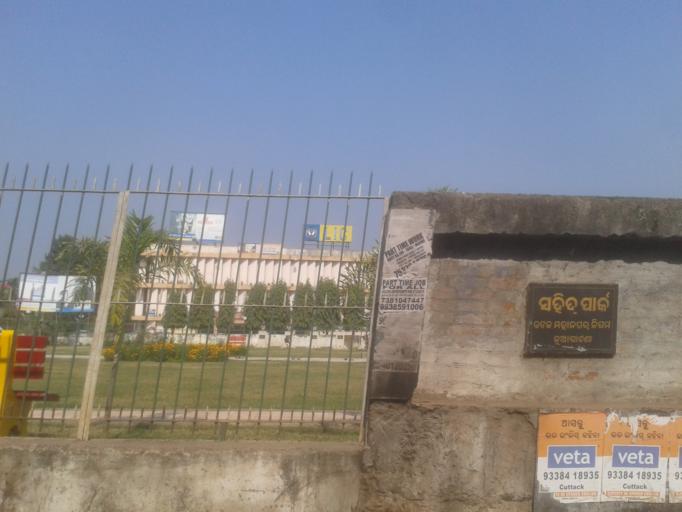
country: IN
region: Odisha
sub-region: Cuttack
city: Cuttack
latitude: 20.4756
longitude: 85.8667
